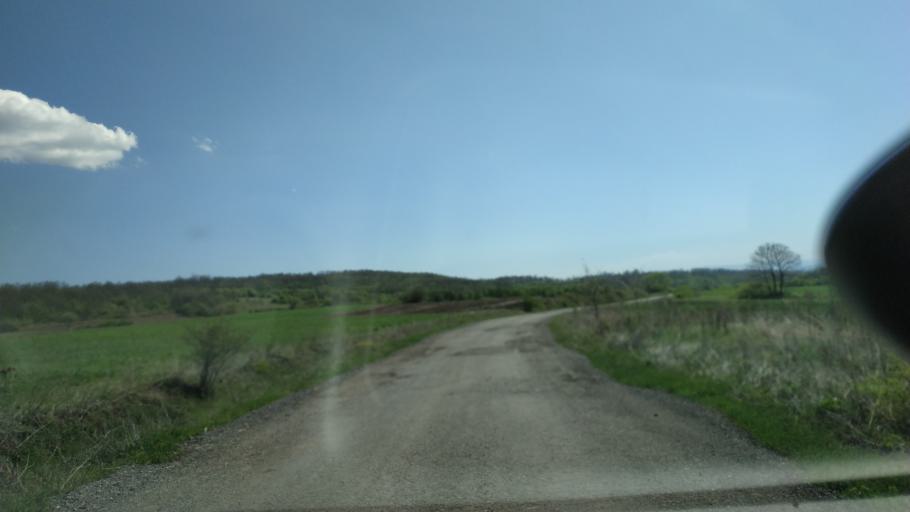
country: RS
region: Central Serbia
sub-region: Zajecarski Okrug
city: Soko Banja
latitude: 43.5147
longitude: 21.9054
